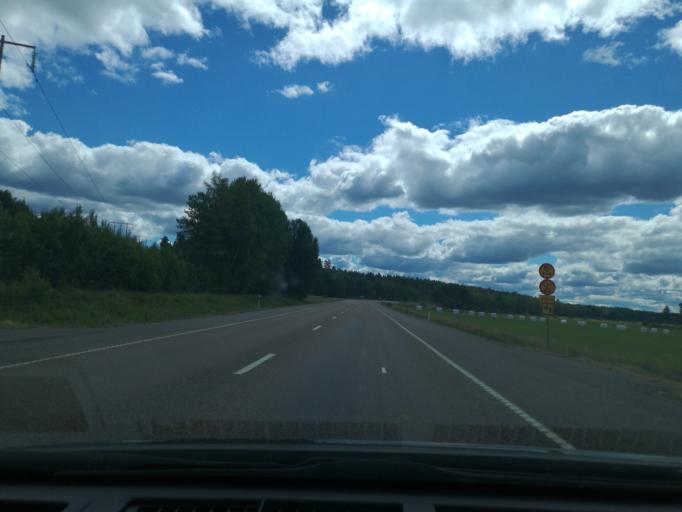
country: SE
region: Vaestmanland
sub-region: Kungsors Kommun
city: Kungsoer
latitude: 59.4036
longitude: 16.1038
